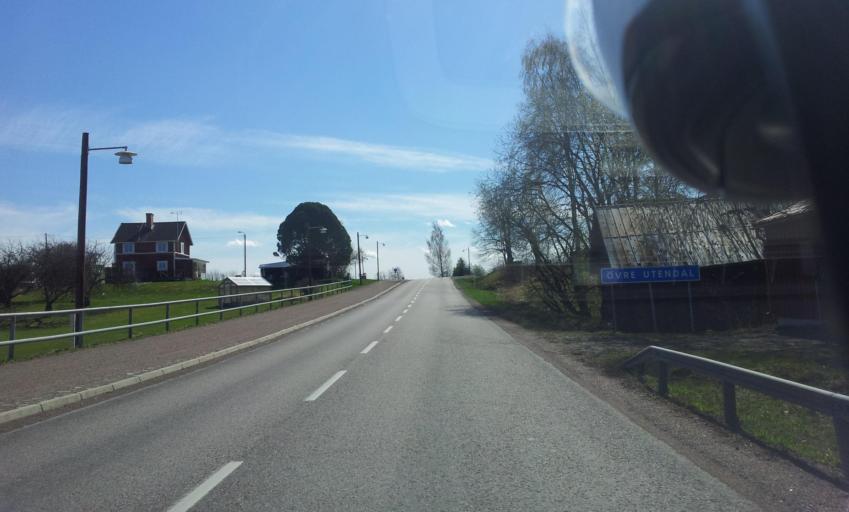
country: SE
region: Dalarna
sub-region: Borlange Kommun
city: Ornas
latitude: 60.4729
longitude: 15.5059
